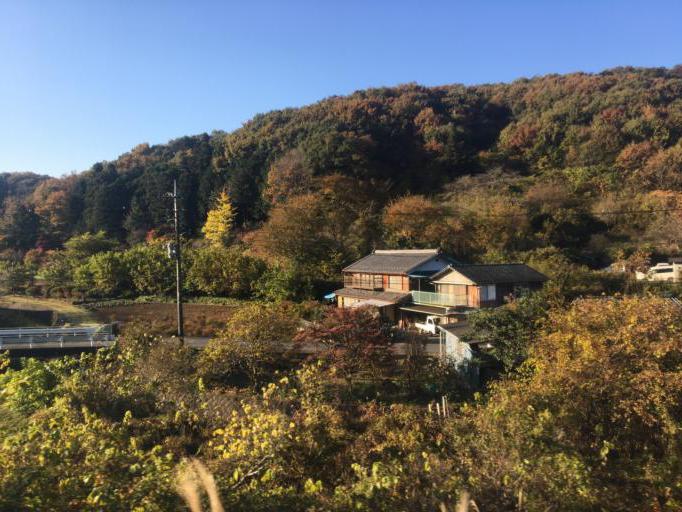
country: JP
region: Saitama
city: Yorii
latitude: 36.0888
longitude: 139.2036
